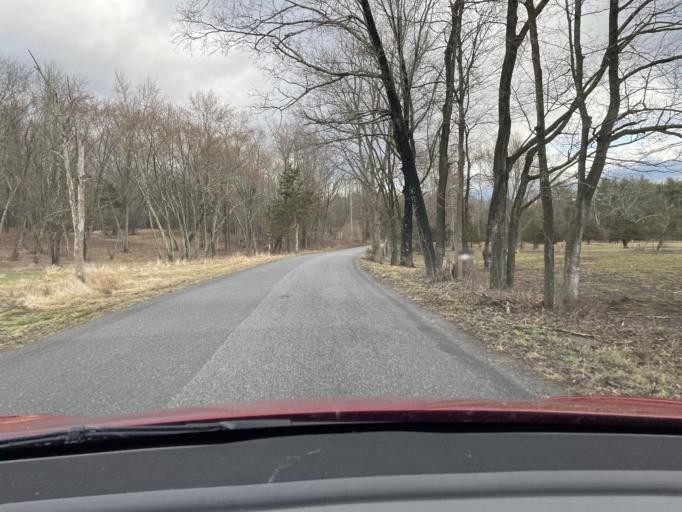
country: US
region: New York
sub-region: Ulster County
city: Manorville
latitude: 42.0767
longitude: -74.0413
